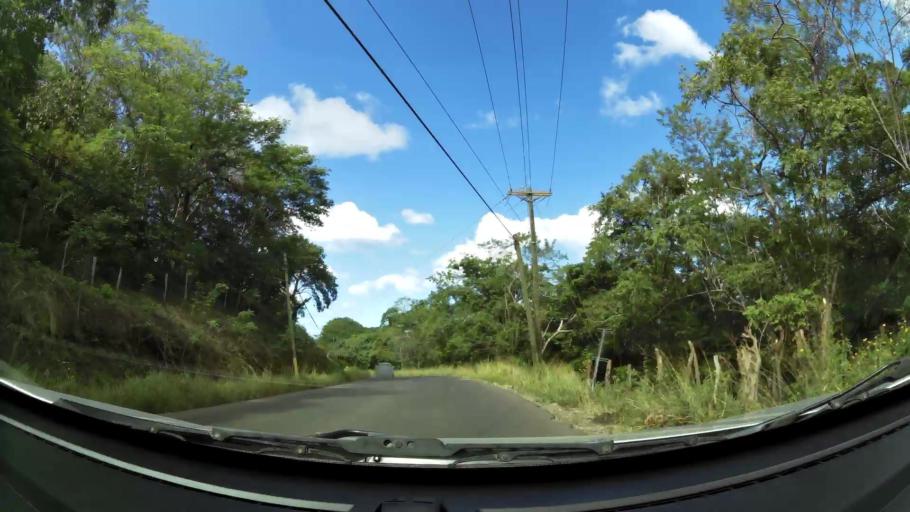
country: CR
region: Guanacaste
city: Santa Cruz
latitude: 10.3108
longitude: -85.8179
